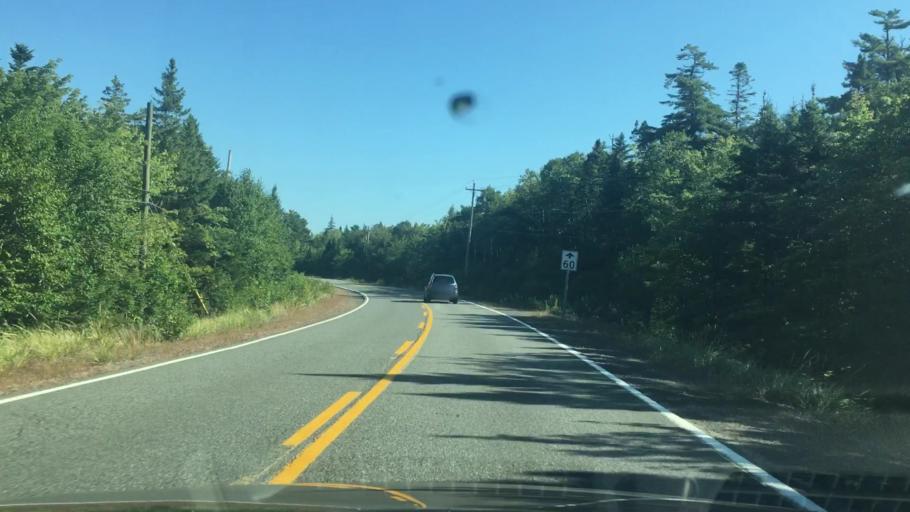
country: CA
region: Nova Scotia
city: Cole Harbour
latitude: 44.8003
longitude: -62.8818
